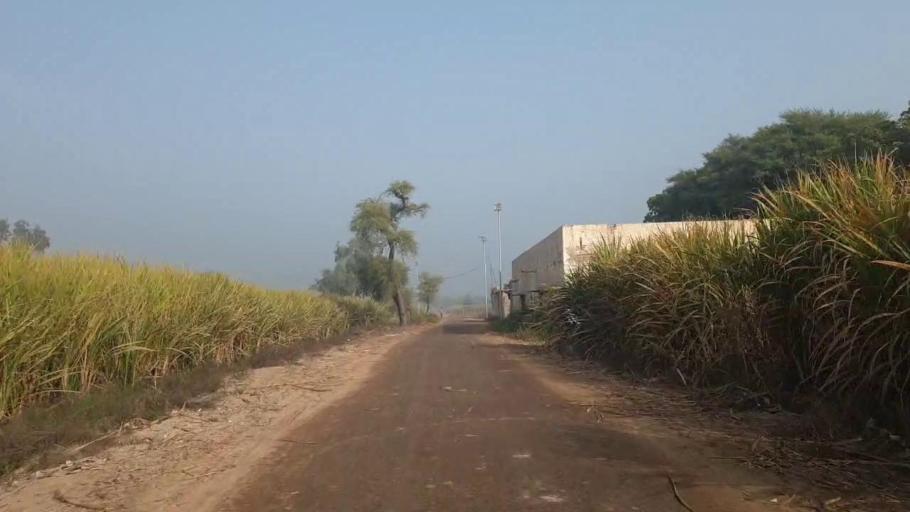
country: PK
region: Sindh
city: Tando Adam
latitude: 25.8003
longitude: 68.6153
